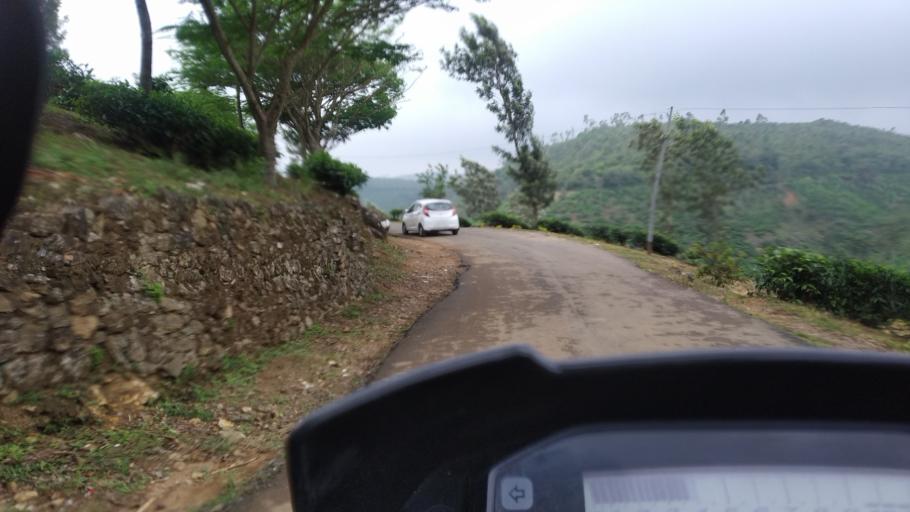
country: IN
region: Tamil Nadu
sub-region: Theni
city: Gudalur
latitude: 9.5824
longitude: 77.0116
